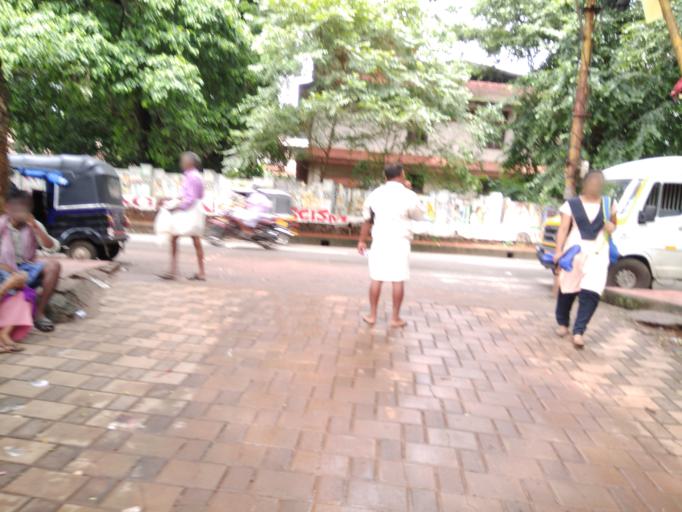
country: IN
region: Kerala
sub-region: Thrissur District
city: Trichur
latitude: 10.5316
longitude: 76.2170
